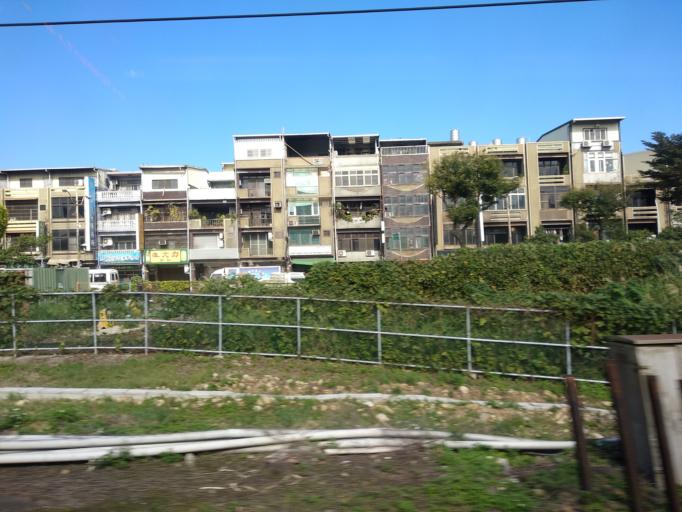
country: TW
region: Taiwan
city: Taoyuan City
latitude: 24.9736
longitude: 121.2616
